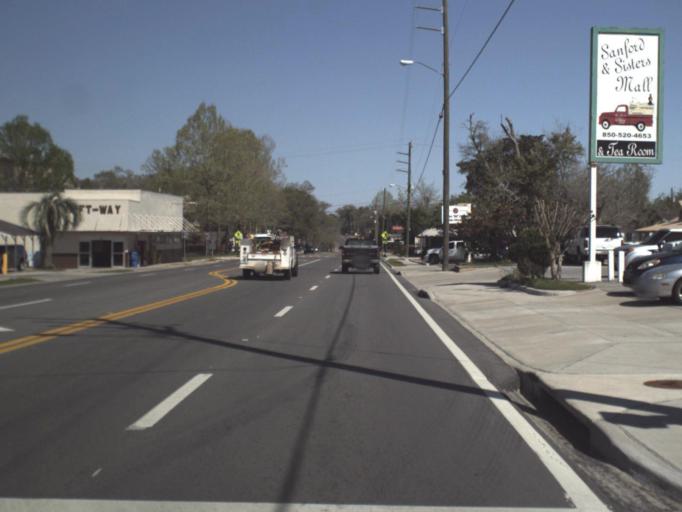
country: US
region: Florida
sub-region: Walton County
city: DeFuniak Springs
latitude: 30.7212
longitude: -86.1129
